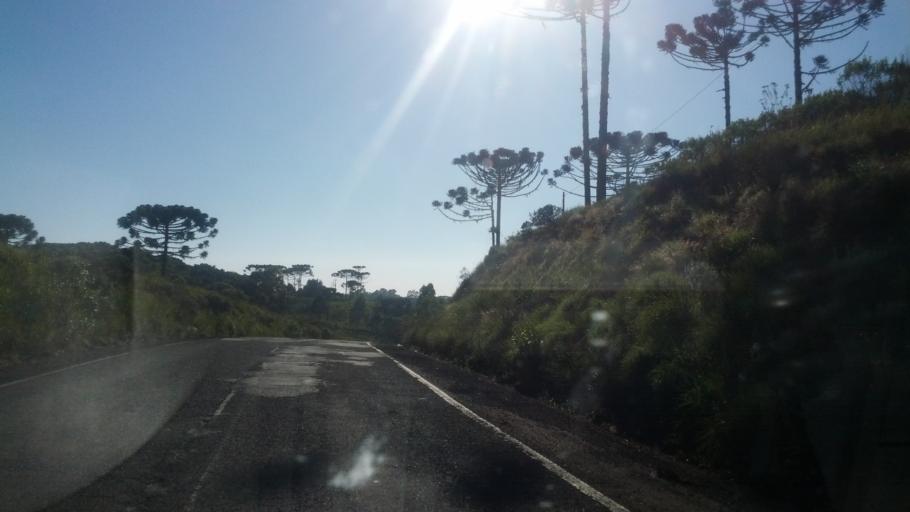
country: BR
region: Santa Catarina
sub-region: Lages
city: Lages
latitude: -27.9133
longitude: -50.5803
